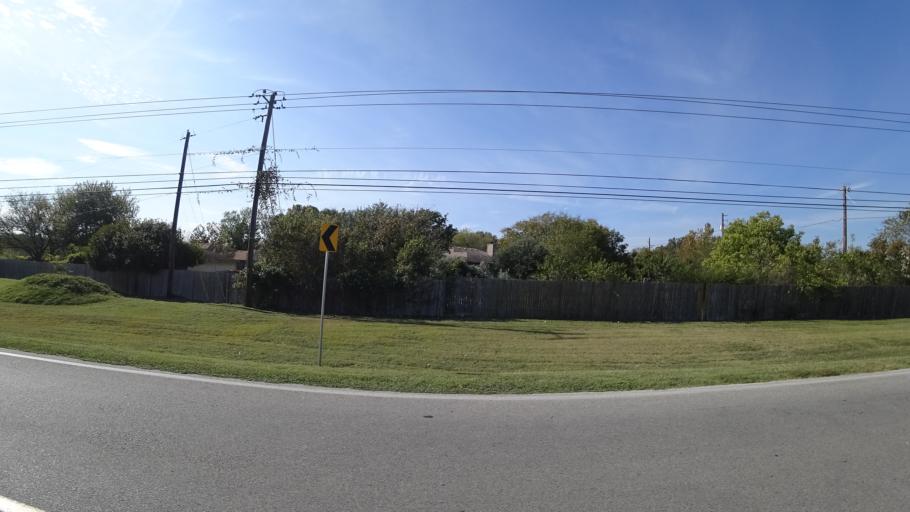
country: US
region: Texas
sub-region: Travis County
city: Pflugerville
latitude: 30.4131
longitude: -97.6243
